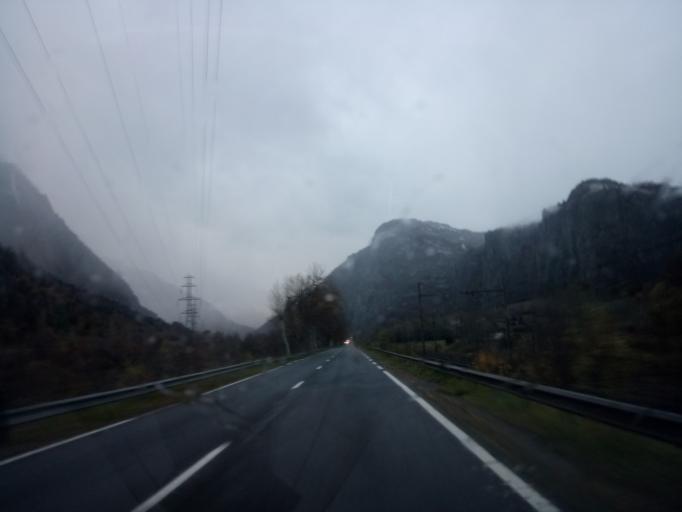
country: FR
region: Rhone-Alpes
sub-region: Departement de la Savoie
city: Saint-Jean-de-Maurienne
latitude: 45.3054
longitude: 6.3477
